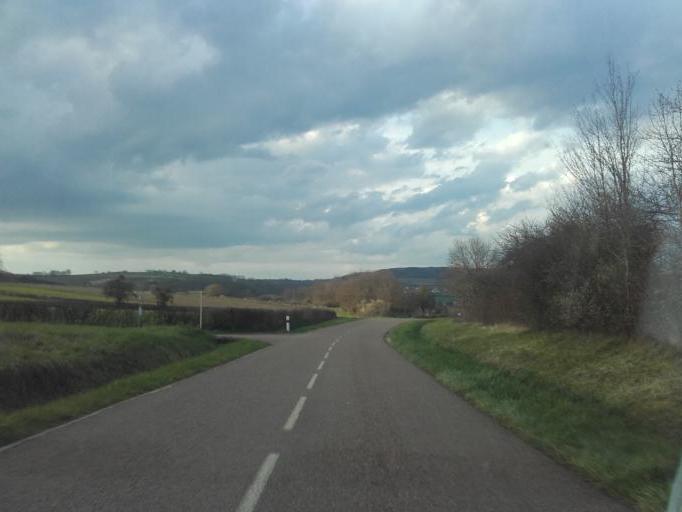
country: FR
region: Bourgogne
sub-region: Departement de la Cote-d'Or
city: Nolay
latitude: 46.9327
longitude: 4.6247
